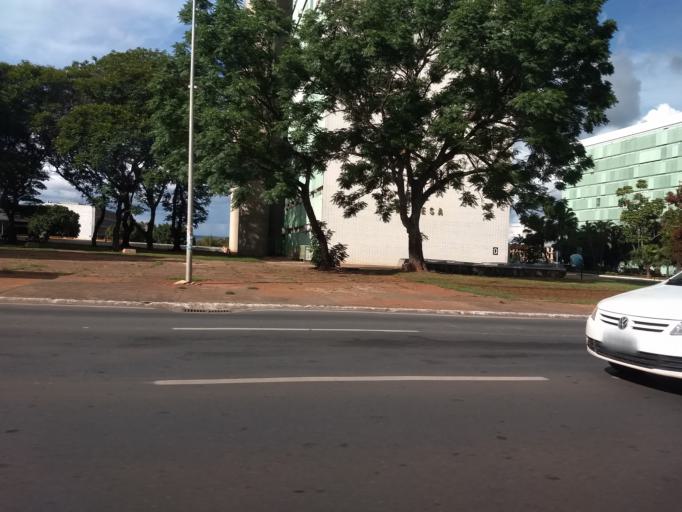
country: BR
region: Federal District
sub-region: Brasilia
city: Brasilia
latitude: -15.7970
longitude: -47.8693
